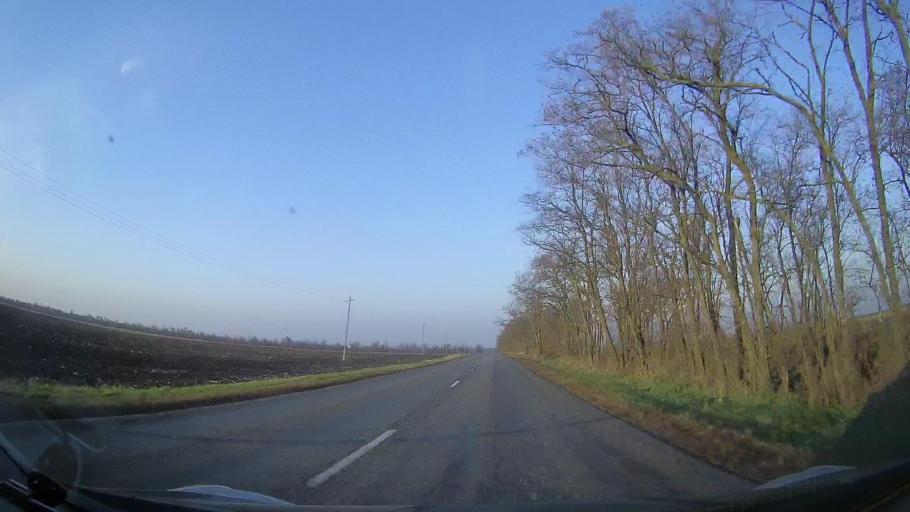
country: RU
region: Rostov
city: Ol'ginskaya
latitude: 47.0938
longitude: 39.9776
